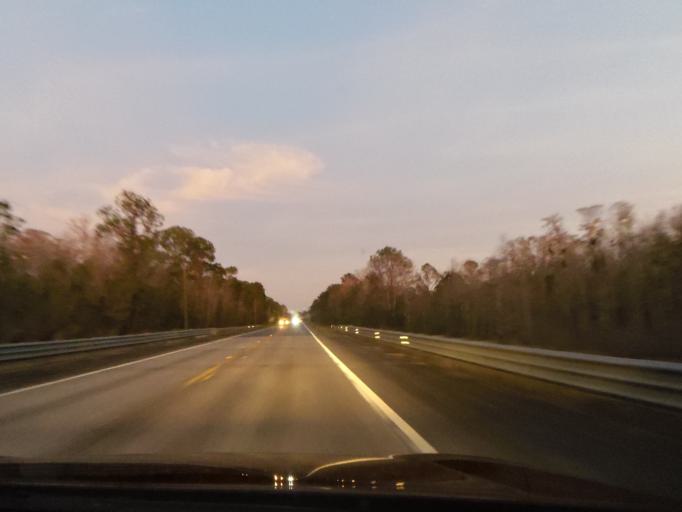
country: US
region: Florida
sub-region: Volusia County
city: De Leon Springs
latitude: 29.2266
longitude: -81.3114
